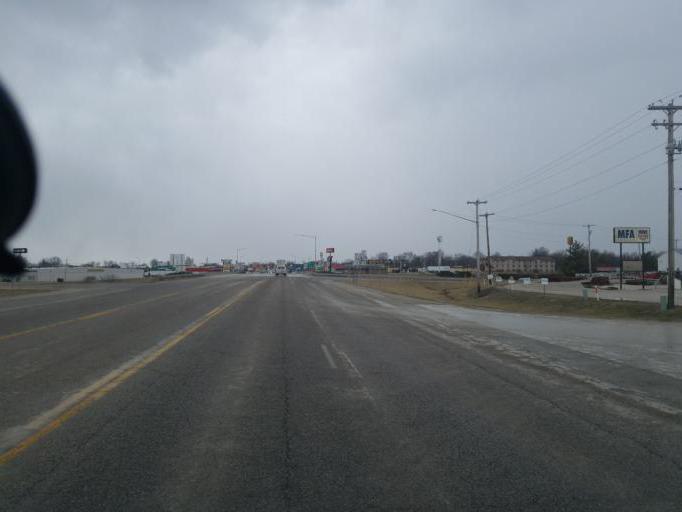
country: US
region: Missouri
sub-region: Macon County
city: Macon
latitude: 39.7557
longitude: -92.4678
